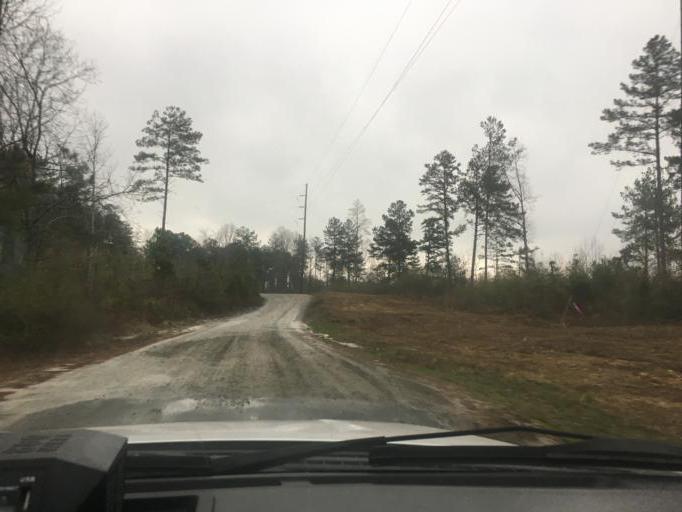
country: US
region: Georgia
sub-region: Dawson County
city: Dawsonville
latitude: 34.4409
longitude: -84.2224
